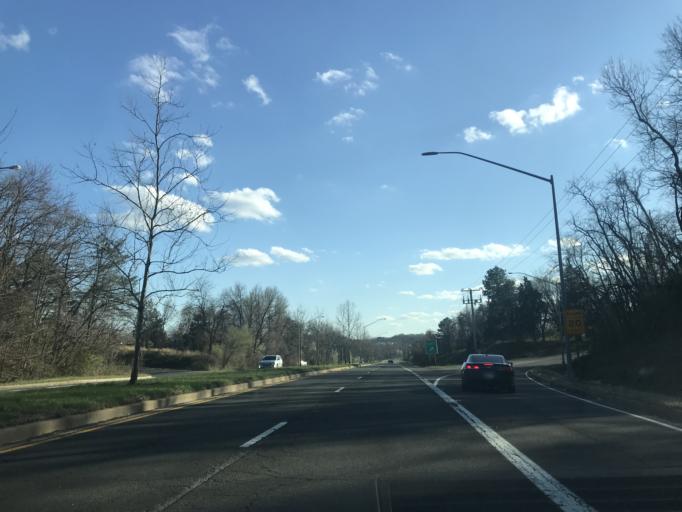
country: US
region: Maryland
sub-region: Prince George's County
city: Glenarden
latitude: 38.9258
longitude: -76.8748
